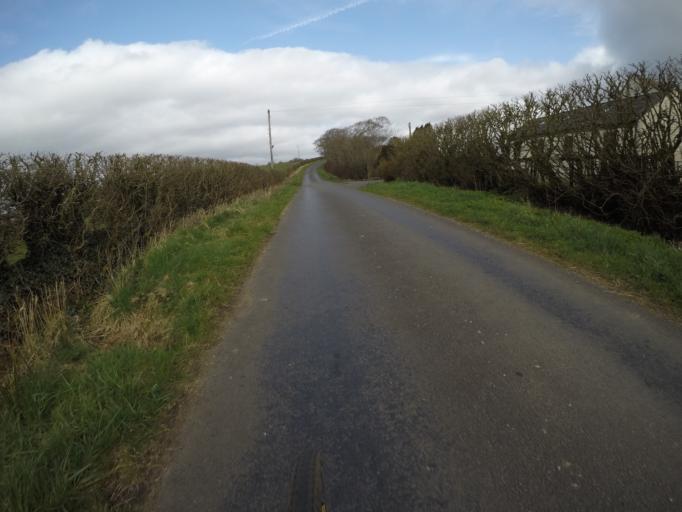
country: GB
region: Scotland
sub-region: North Ayrshire
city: Springside
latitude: 55.6562
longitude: -4.6100
